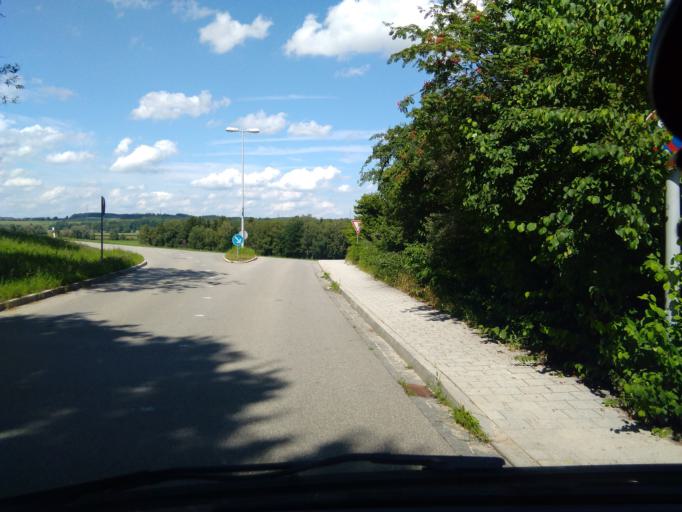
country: DE
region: Bavaria
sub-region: Upper Bavaria
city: Assling
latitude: 47.9929
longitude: 11.9930
